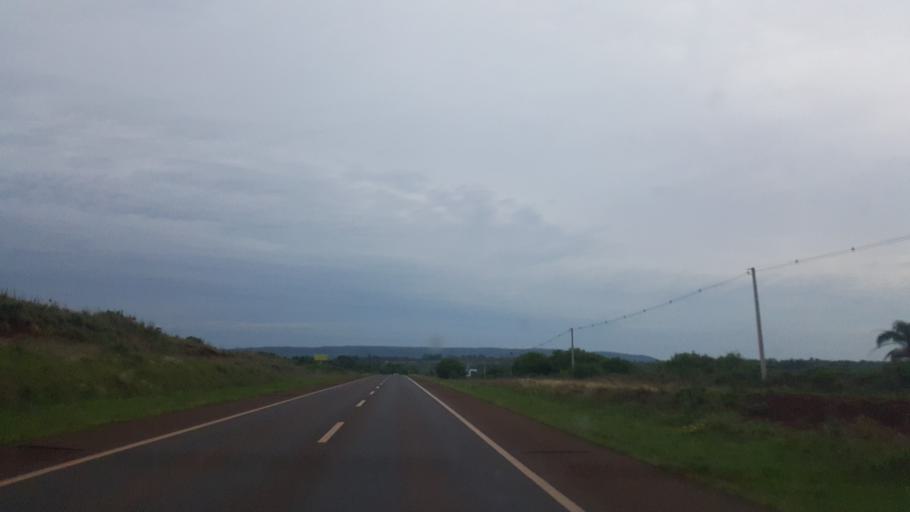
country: AR
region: Misiones
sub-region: Departamento de Apostoles
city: San Jose
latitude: -27.7710
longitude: -55.8052
